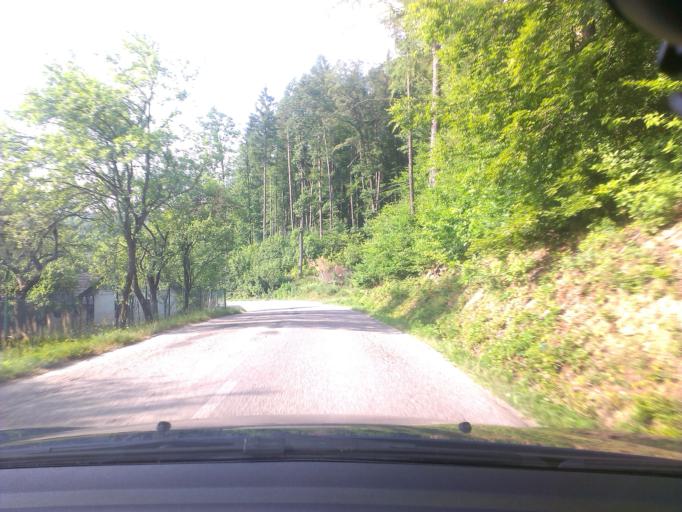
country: SK
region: Trenciansky
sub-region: Okres Myjava
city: Myjava
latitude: 48.7997
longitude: 17.5902
